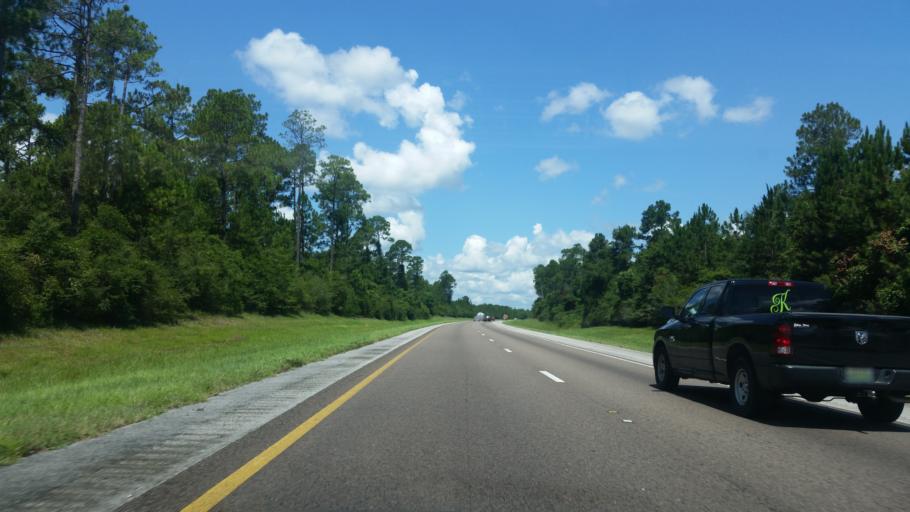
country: US
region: Alabama
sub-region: Baldwin County
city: Robertsdale
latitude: 30.5875
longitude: -87.5330
